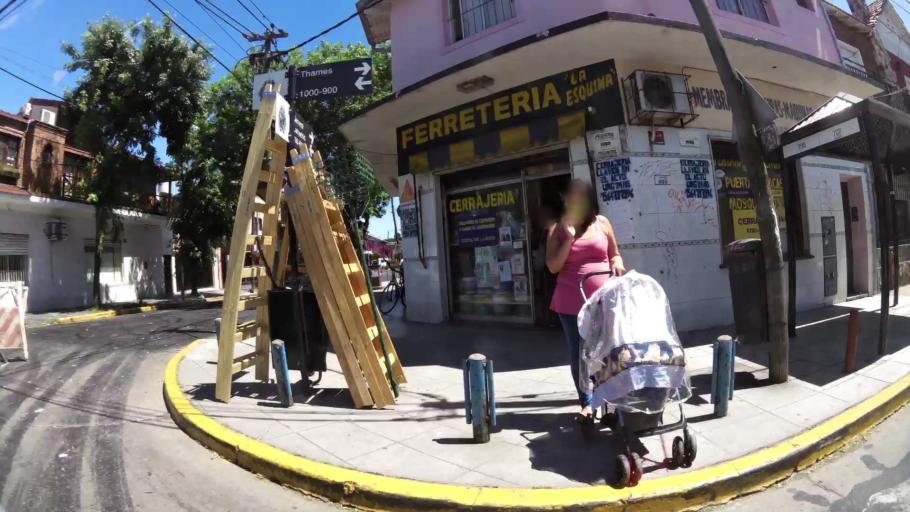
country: AR
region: Buenos Aires
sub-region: Partido de San Isidro
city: San Isidro
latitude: -34.5048
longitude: -58.5501
